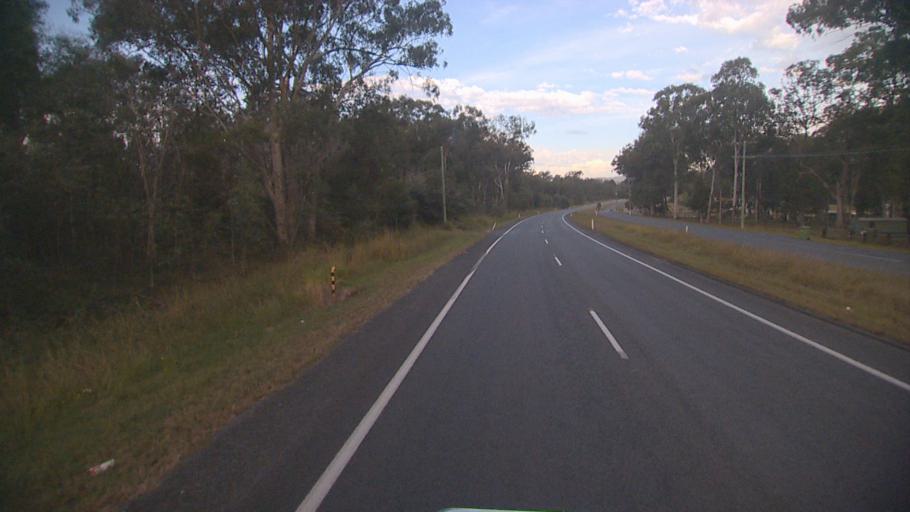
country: AU
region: Queensland
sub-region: Logan
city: Cedar Vale
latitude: -27.8398
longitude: 153.1140
